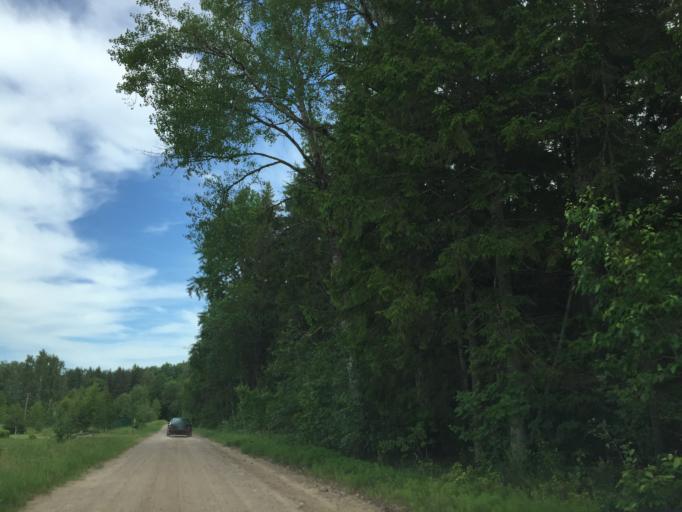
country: LV
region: Engure
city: Smarde
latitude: 57.0256
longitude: 23.2565
